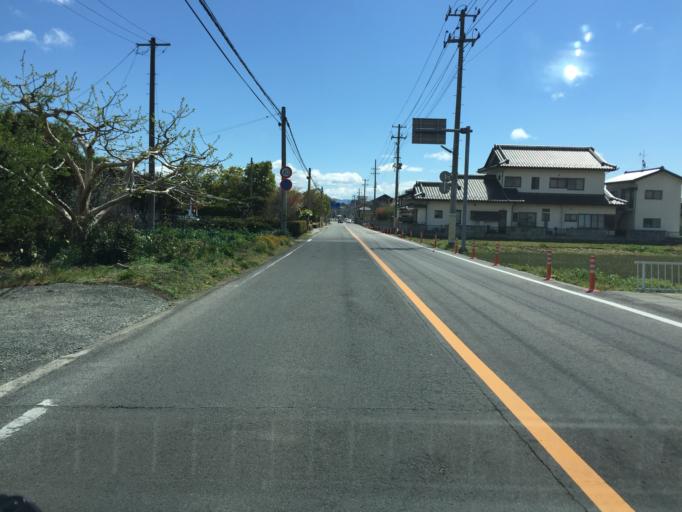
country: JP
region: Fukushima
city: Fukushima-shi
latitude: 37.8396
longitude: 140.4428
